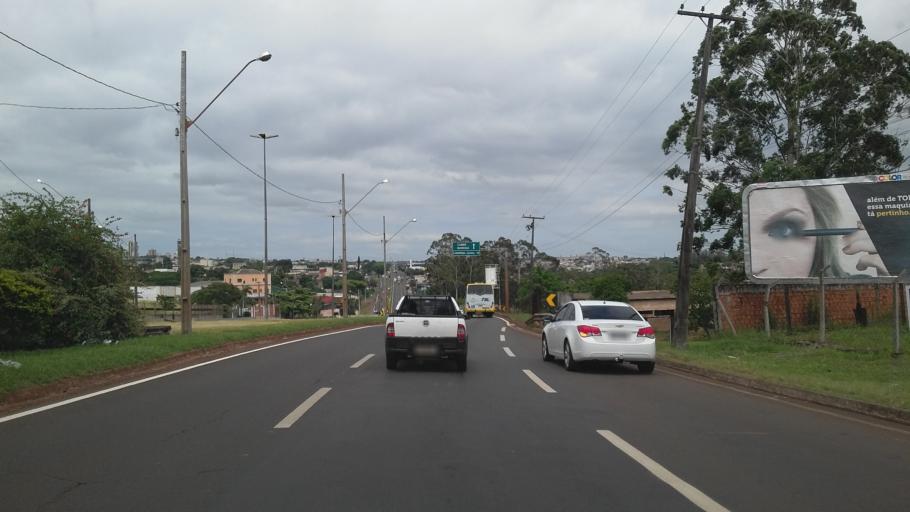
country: BR
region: Parana
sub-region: Londrina
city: Londrina
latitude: -23.2929
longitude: -51.1454
